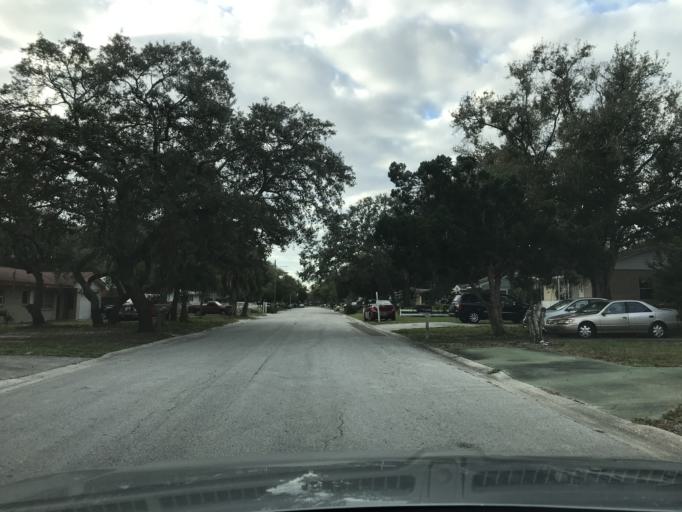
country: US
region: Florida
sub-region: Pinellas County
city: Clearwater
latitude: 27.9494
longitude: -82.7850
